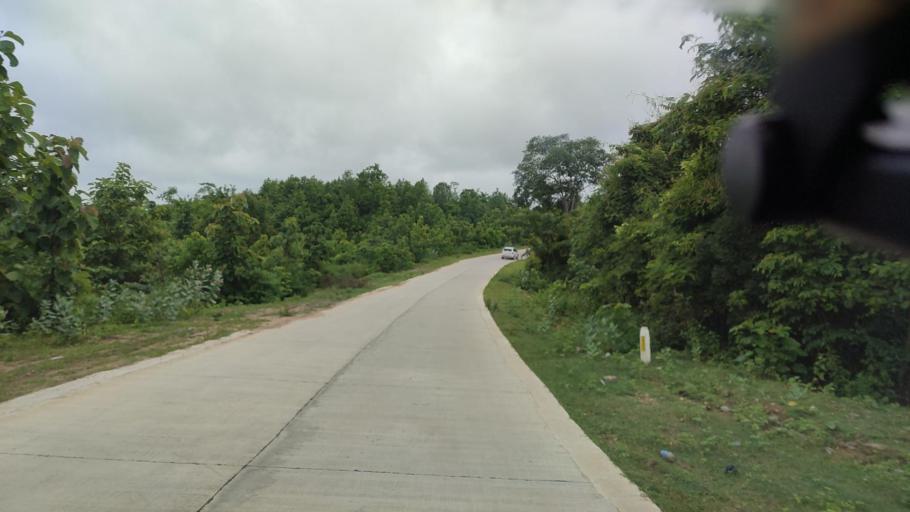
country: MM
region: Magway
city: Taungdwingyi
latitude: 20.0178
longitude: 95.8107
